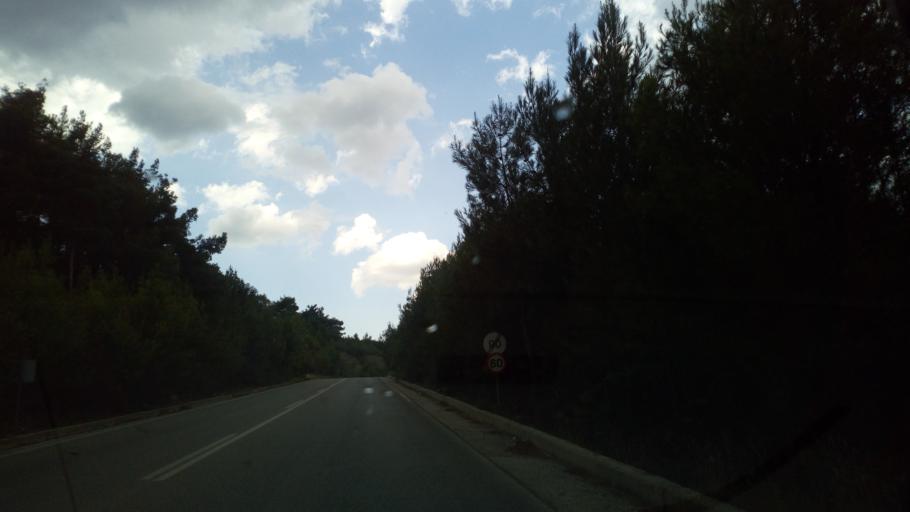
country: GR
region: Central Macedonia
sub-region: Nomos Chalkidikis
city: Polygyros
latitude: 40.3567
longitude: 23.4406
